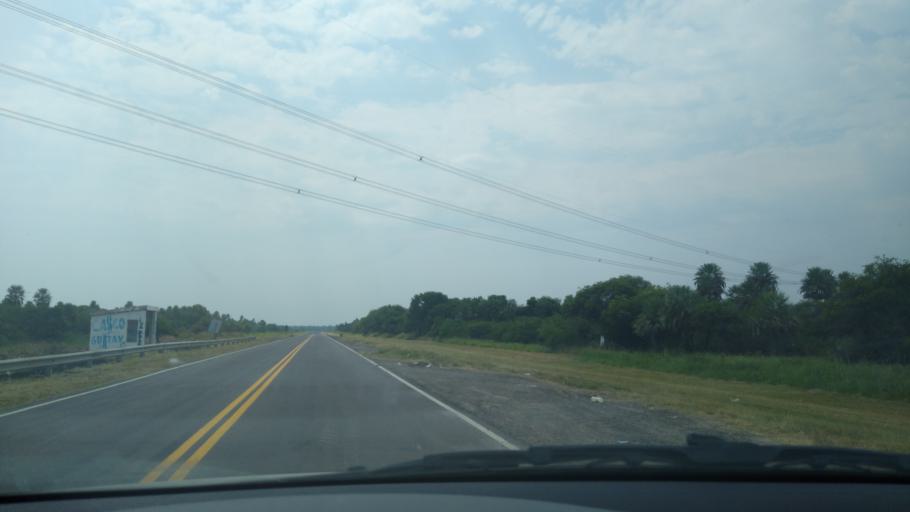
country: AR
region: Chaco
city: Margarita Belen
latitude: -27.0842
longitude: -58.9593
